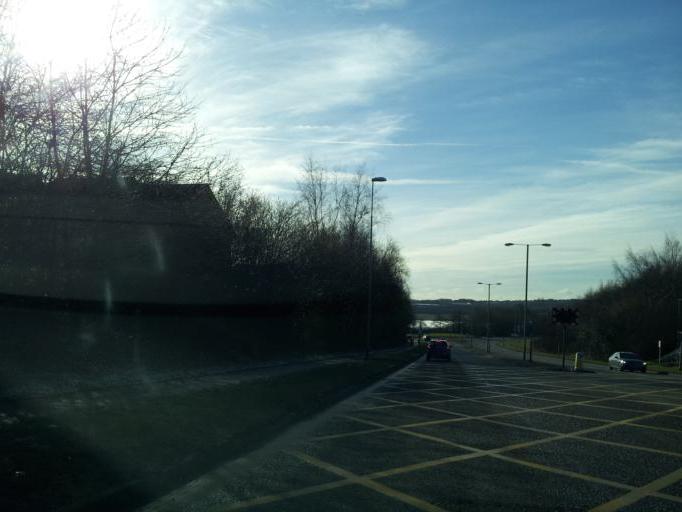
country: GB
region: England
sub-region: Staffordshire
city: Kidsgrove
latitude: 53.0673
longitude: -2.2193
